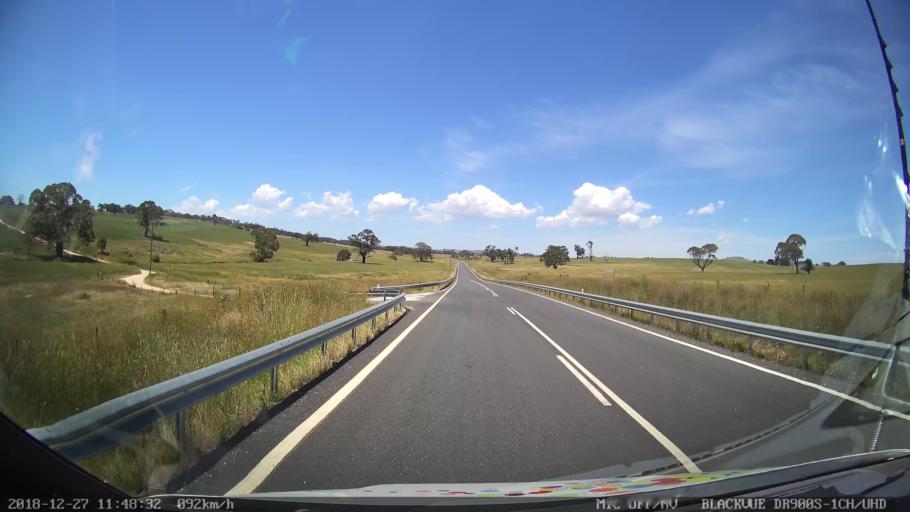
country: AU
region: New South Wales
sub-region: Bathurst Regional
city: Perthville
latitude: -33.6076
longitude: 149.4357
